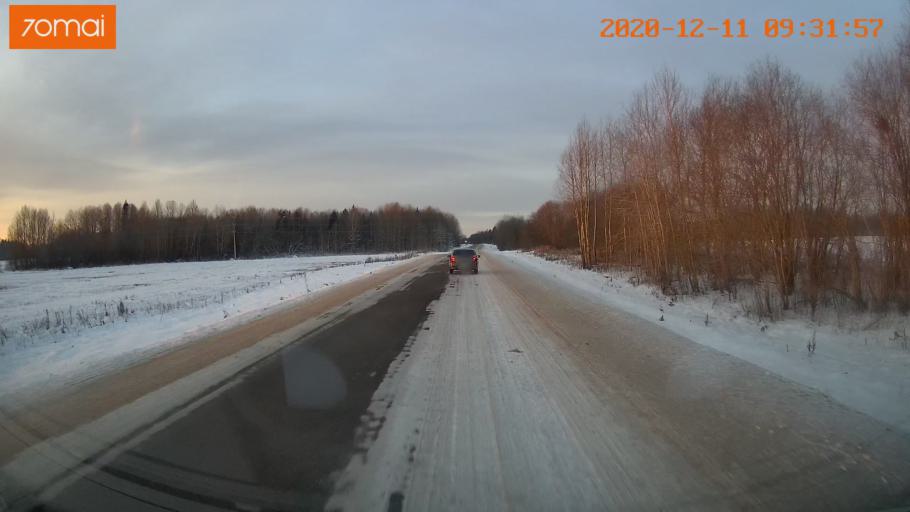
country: RU
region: Vologda
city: Vologda
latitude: 59.1255
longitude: 39.9757
